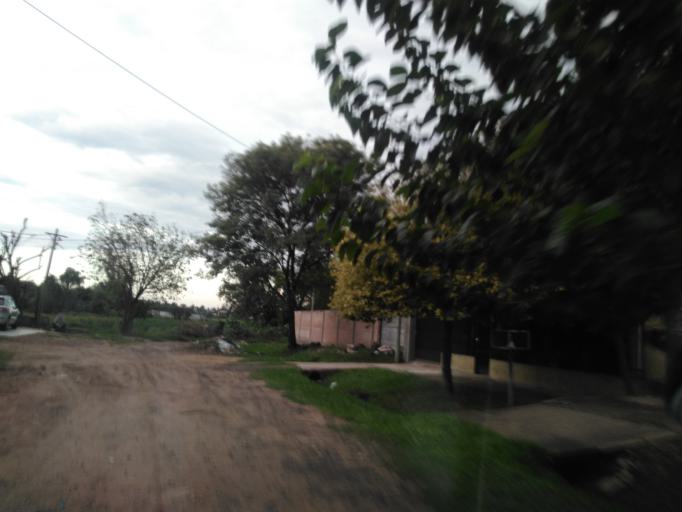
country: AR
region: Chaco
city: Resistencia
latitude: -27.4429
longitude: -58.9720
